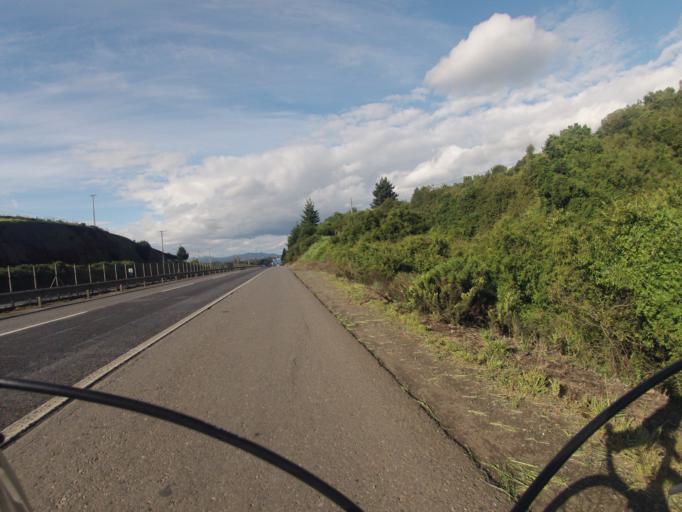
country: CL
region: Araucania
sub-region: Provincia de Cautin
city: Temuco
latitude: -38.8027
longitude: -72.6257
